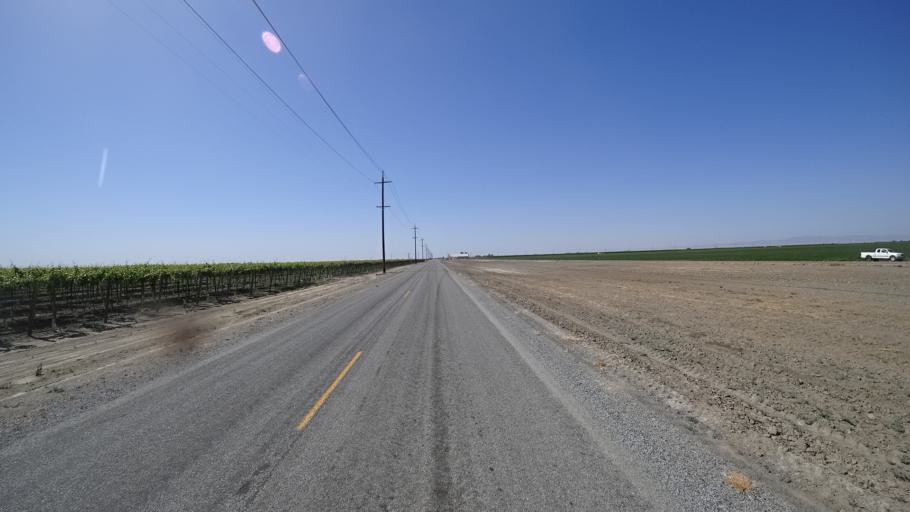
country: US
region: California
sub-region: Kings County
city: Stratford
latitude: 36.2376
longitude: -119.8344
